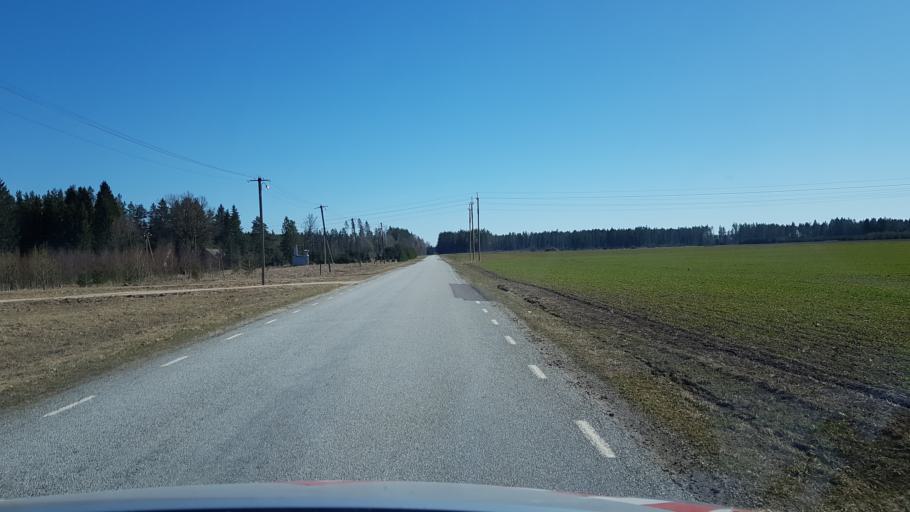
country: EE
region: Laeaene-Virumaa
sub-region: Viru-Nigula vald
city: Kunda
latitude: 59.3899
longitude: 26.5701
